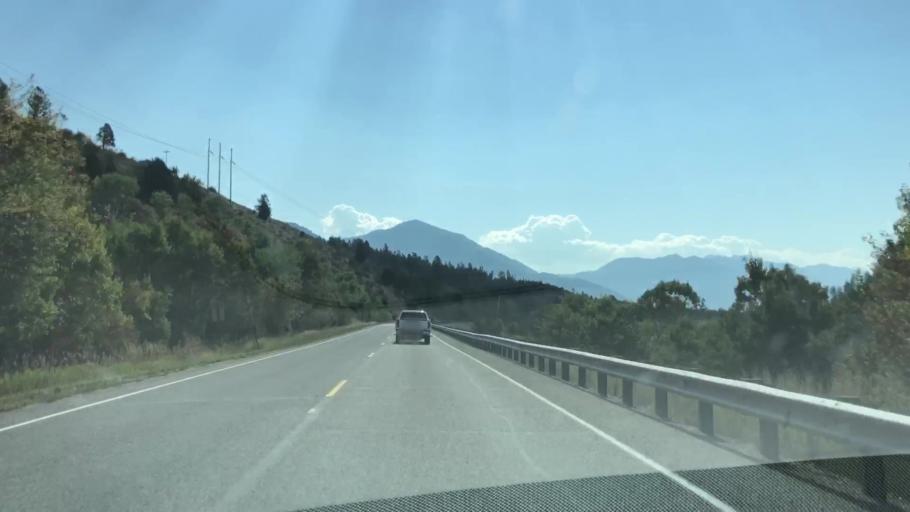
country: US
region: Wyoming
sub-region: Teton County
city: Hoback
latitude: 43.2051
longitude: -111.0502
